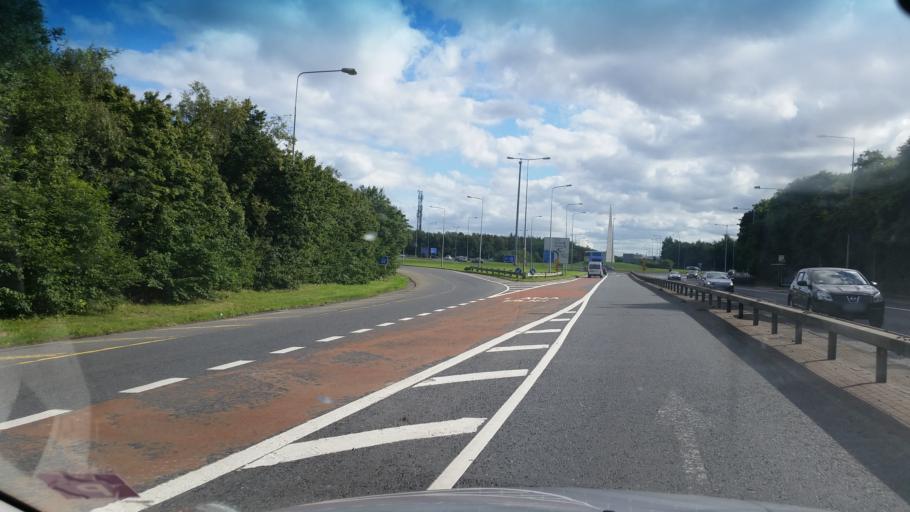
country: IE
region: Leinster
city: Kinsealy-Drinan
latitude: 53.4303
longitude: -6.2300
